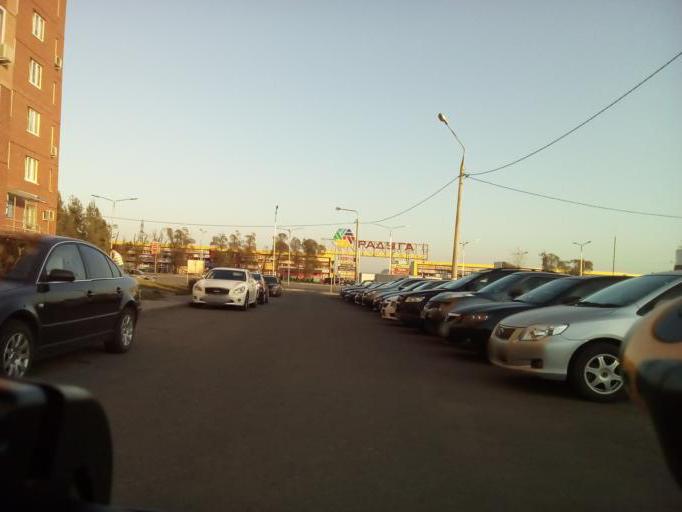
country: RU
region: Moskovskaya
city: Ramenskoye
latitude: 55.5913
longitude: 38.2510
